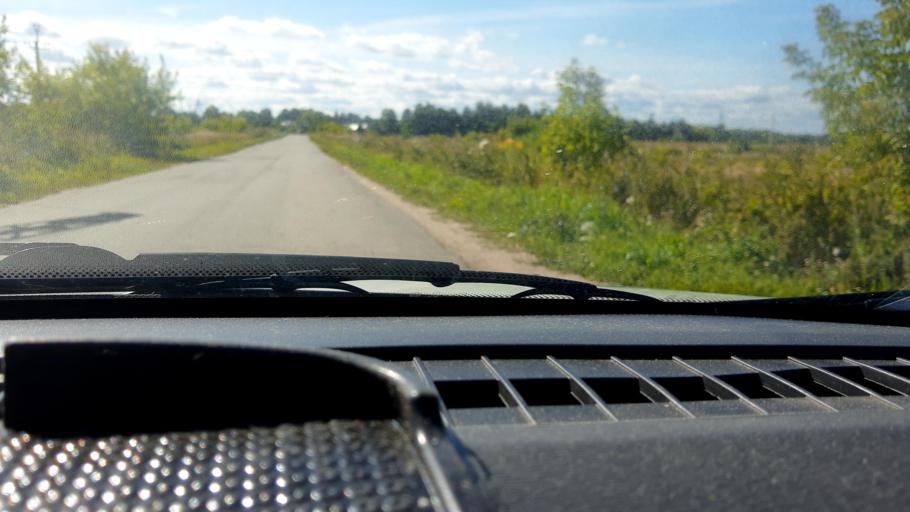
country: RU
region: Nizjnij Novgorod
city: Lukino
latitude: 56.4378
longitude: 43.6725
